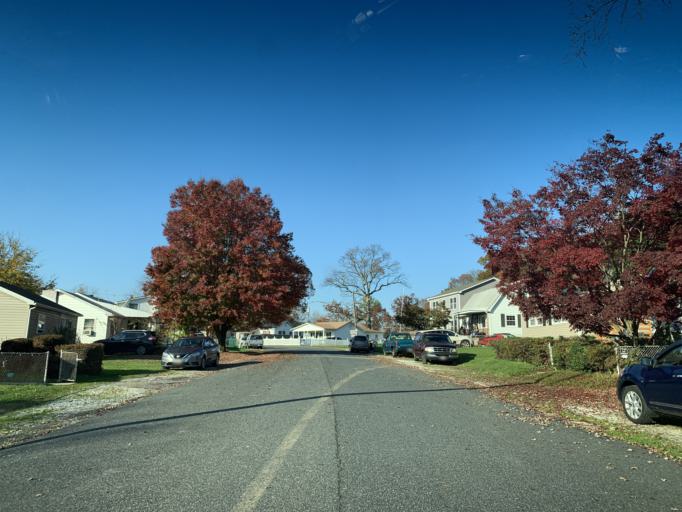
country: US
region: Maryland
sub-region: Baltimore County
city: Middle River
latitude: 39.3393
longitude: -76.4540
